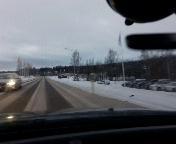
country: SE
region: Gaevleborg
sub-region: Bollnas Kommun
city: Bollnas
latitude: 61.3420
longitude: 16.3858
